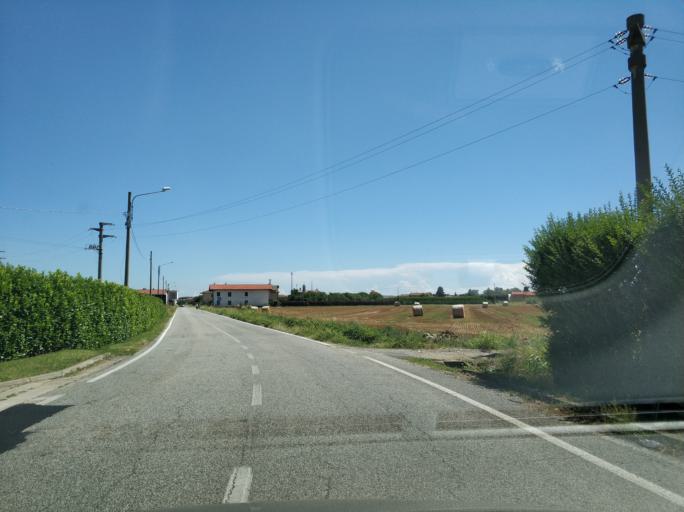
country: IT
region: Piedmont
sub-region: Provincia di Vercelli
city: Cigliano
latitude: 45.3194
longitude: 8.0175
